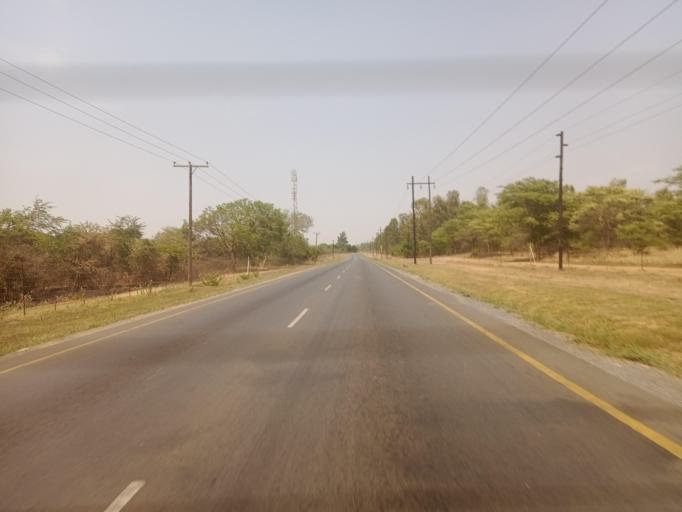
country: ZM
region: Lusaka
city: Lusaka
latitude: -15.2852
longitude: 28.3832
